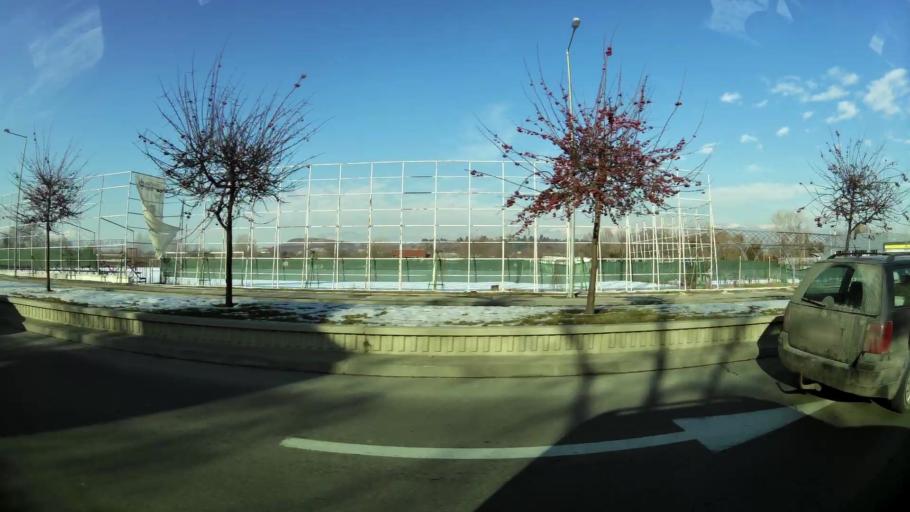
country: MK
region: Karpos
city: Skopje
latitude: 42.0074
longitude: 21.3990
